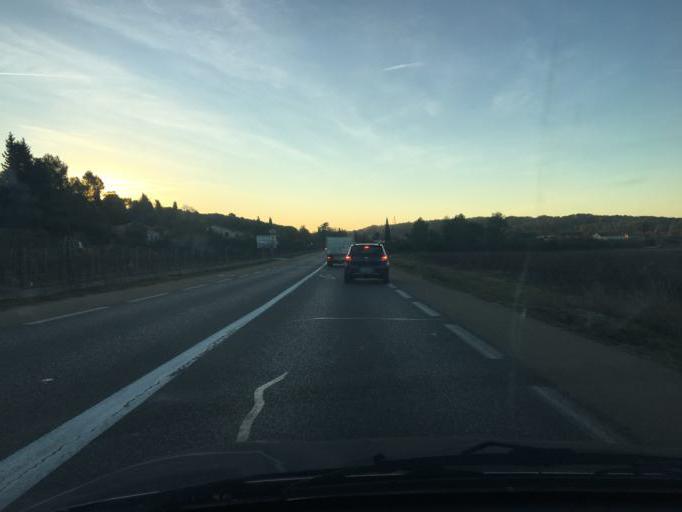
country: FR
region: Provence-Alpes-Cote d'Azur
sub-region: Departement du Var
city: Lorgues
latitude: 43.4853
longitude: 6.3672
